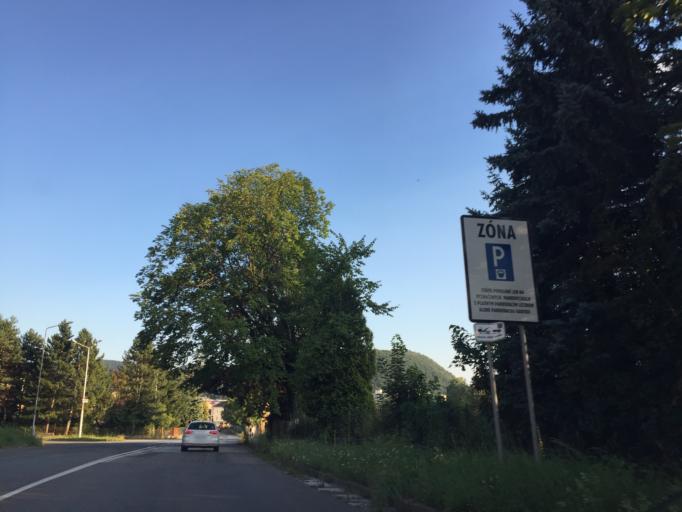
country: SK
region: Banskobystricky
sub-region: Okres Banska Bystrica
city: Banska Bystrica
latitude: 48.7405
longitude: 19.1406
